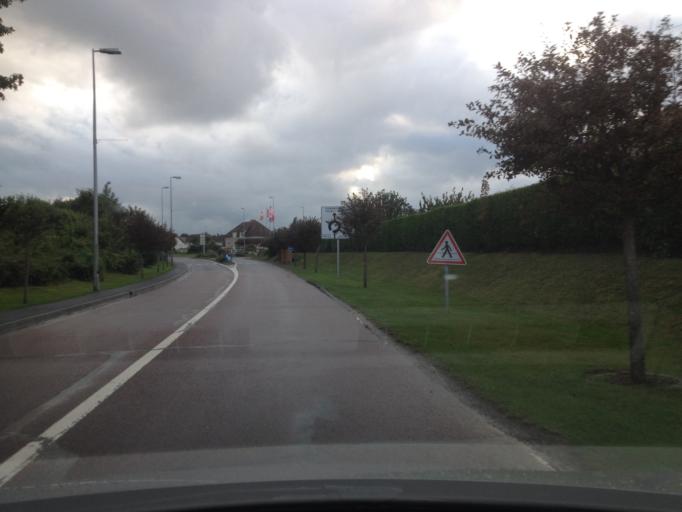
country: FR
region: Lower Normandy
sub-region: Departement du Calvados
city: Grandcamp-Maisy
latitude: 49.3863
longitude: -1.0482
